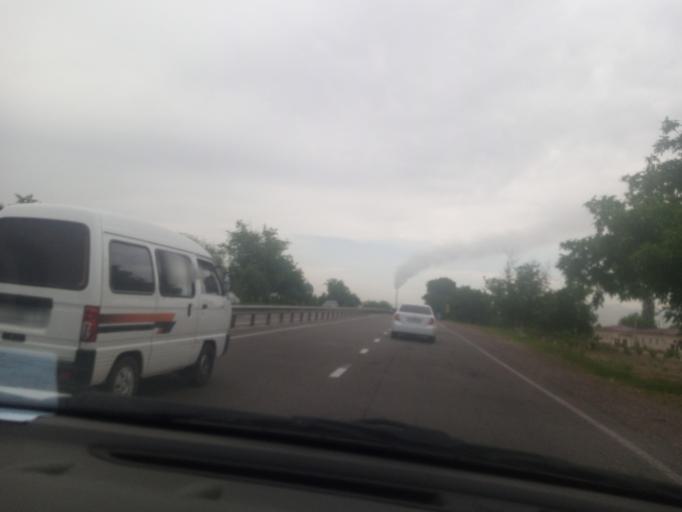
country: UZ
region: Toshkent
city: Ohangaron
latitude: 40.9043
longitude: 69.7259
